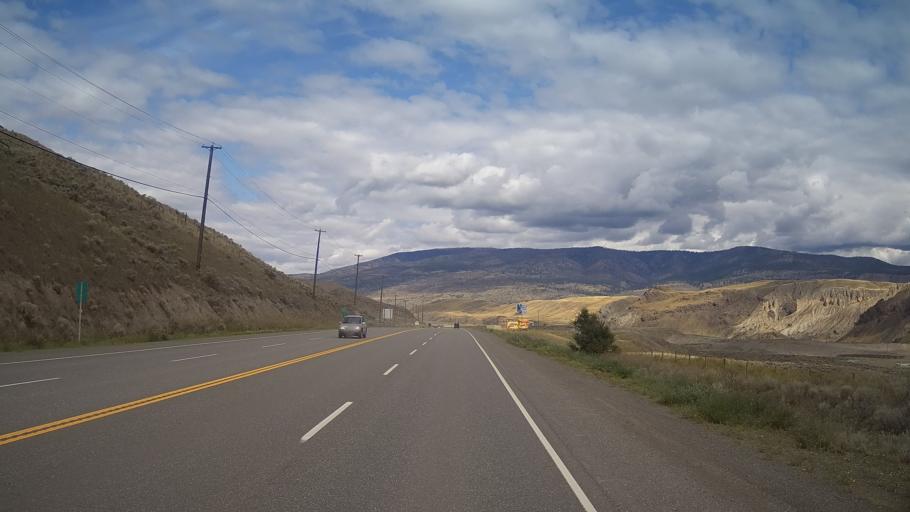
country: CA
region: British Columbia
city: Cache Creek
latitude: 50.7772
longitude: -121.3126
